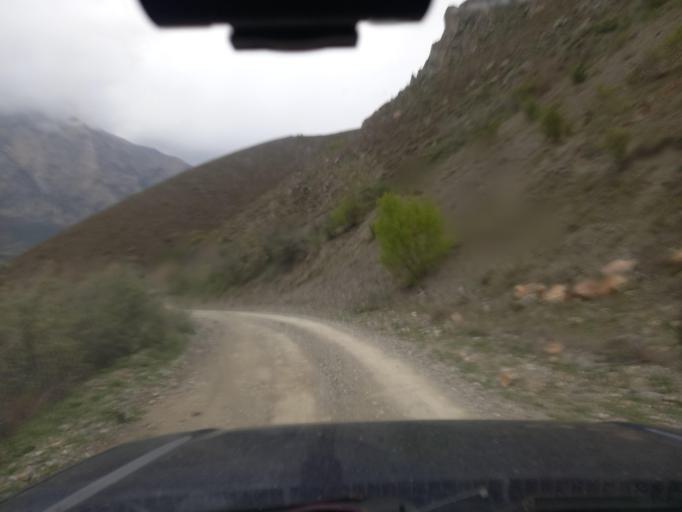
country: RU
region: North Ossetia
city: Mizur
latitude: 42.8538
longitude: 44.1620
